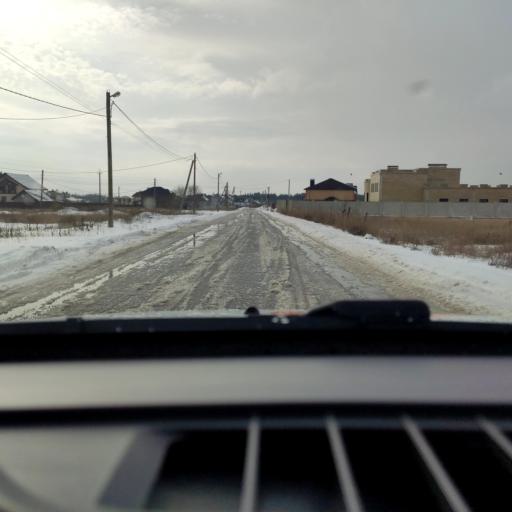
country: RU
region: Voronezj
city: Podgornoye
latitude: 51.7735
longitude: 39.1249
